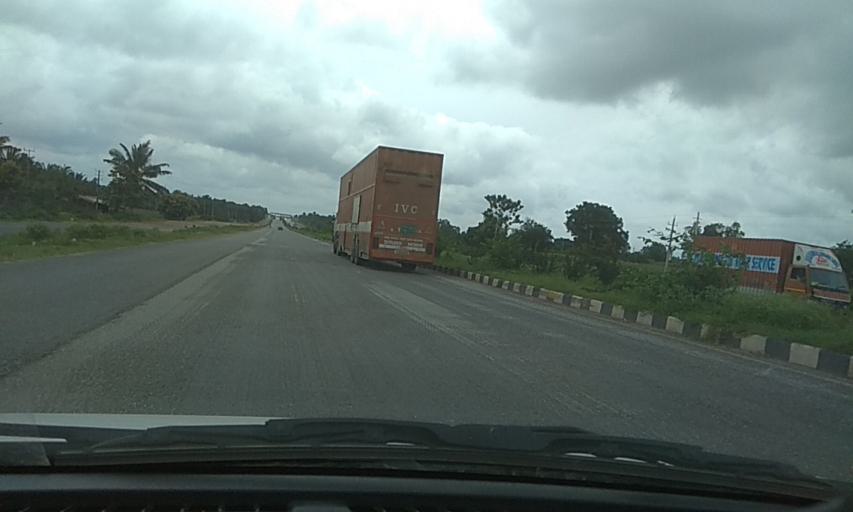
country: IN
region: Karnataka
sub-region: Davanagere
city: Mayakonda
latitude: 14.3691
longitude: 76.1377
